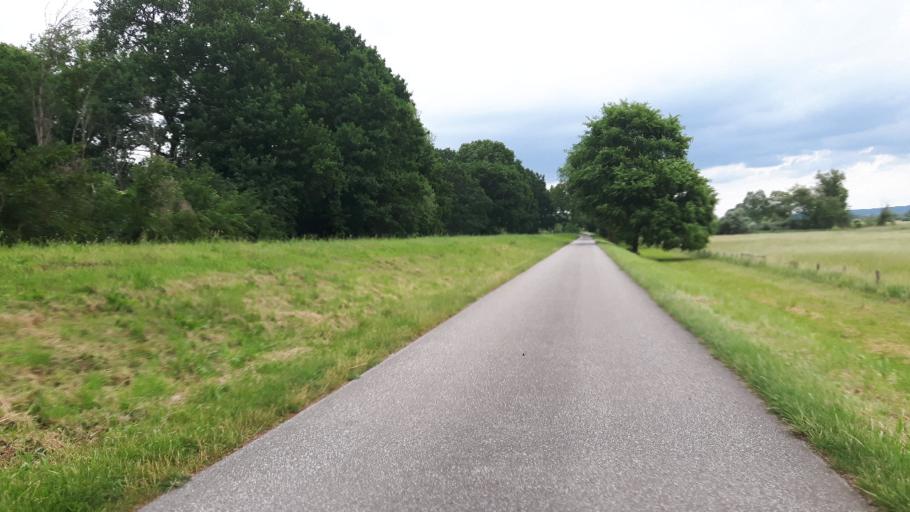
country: DE
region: Brandenburg
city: Schoneberg
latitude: 52.9848
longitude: 14.1390
